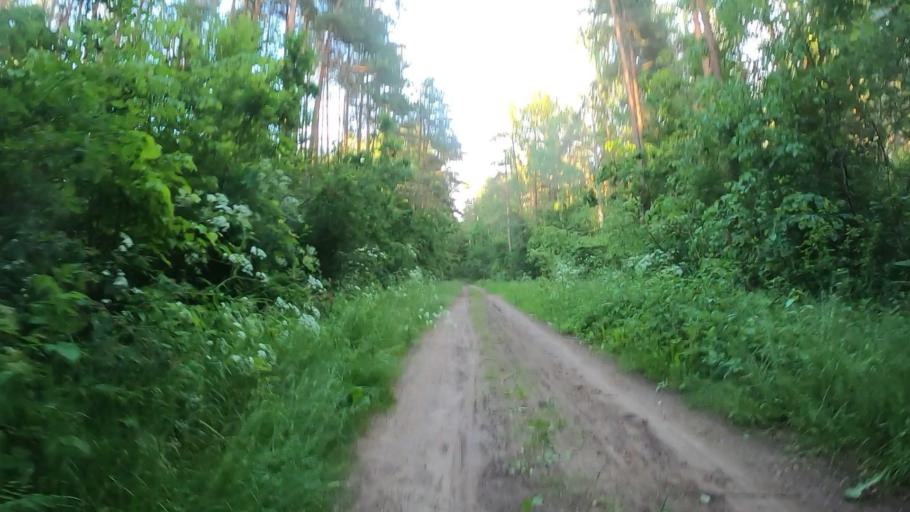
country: LV
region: Marupe
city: Marupe
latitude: 56.8783
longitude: 24.0097
